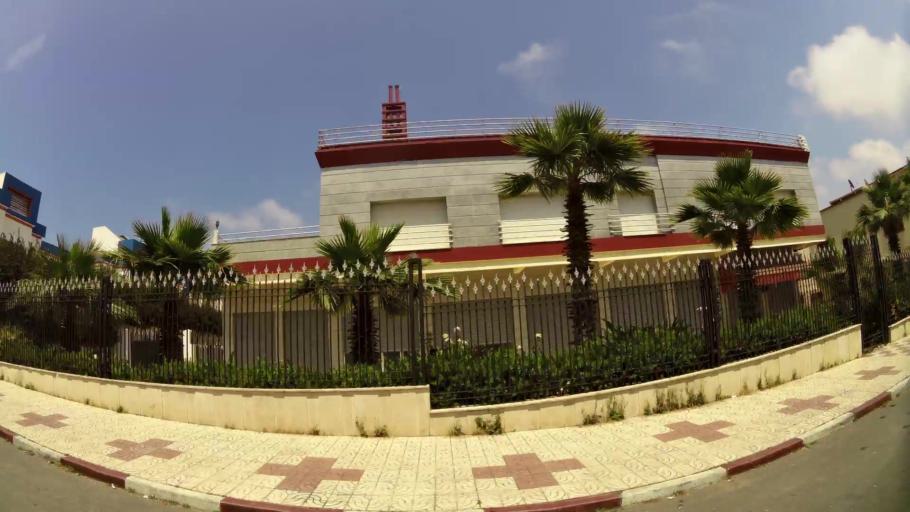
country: MA
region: Rabat-Sale-Zemmour-Zaer
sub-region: Skhirate-Temara
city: Temara
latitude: 33.9731
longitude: -6.8932
